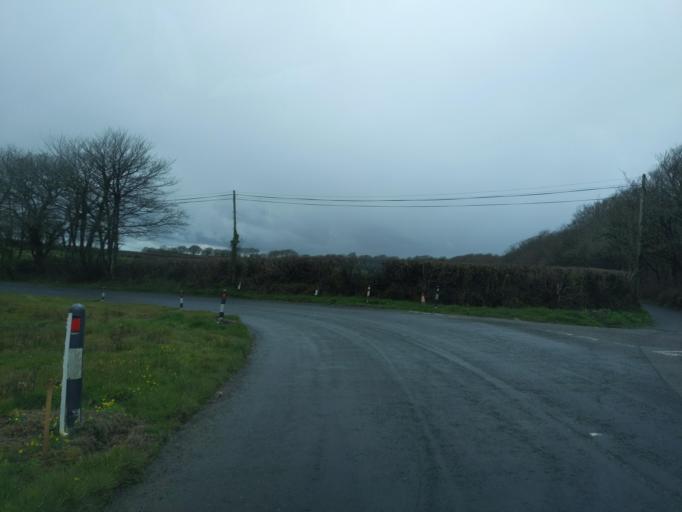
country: GB
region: England
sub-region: Cornwall
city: North Hill
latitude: 50.5878
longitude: -4.4362
